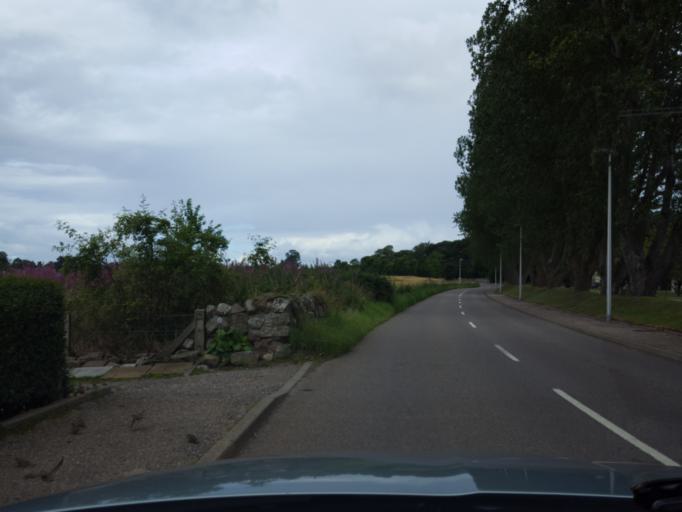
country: GB
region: Scotland
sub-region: Moray
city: Kinloss
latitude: 57.6325
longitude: -3.5604
